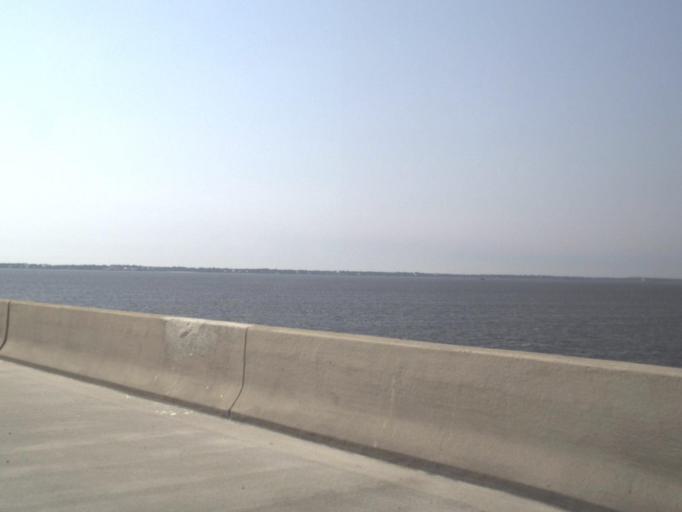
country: US
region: Florida
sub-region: Franklin County
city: Eastpoint
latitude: 29.6911
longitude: -84.8868
